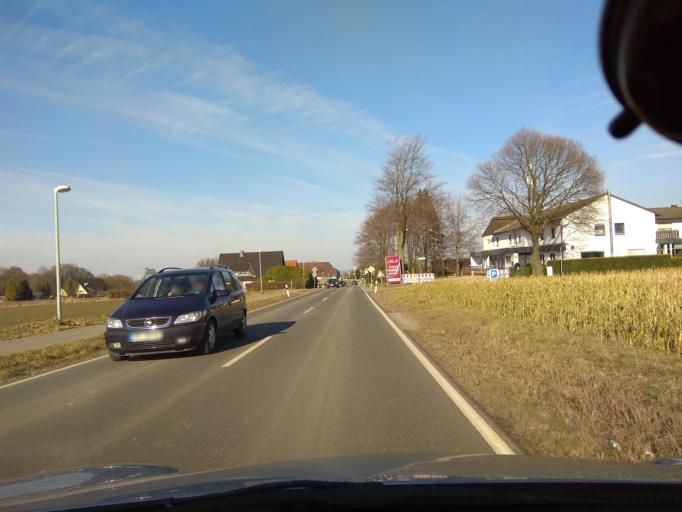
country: DE
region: North Rhine-Westphalia
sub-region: Regierungsbezirk Munster
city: Mettingen
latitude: 52.3026
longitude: 7.7771
